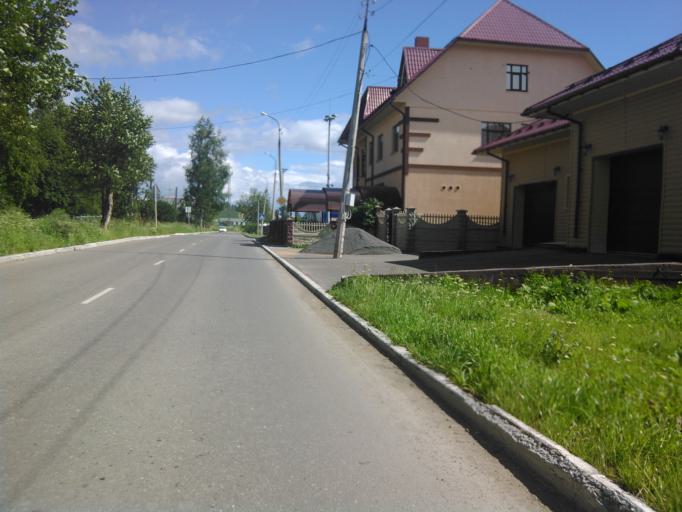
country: RU
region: Sverdlovsk
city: Krasnotur'insk
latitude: 59.7590
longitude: 60.1897
